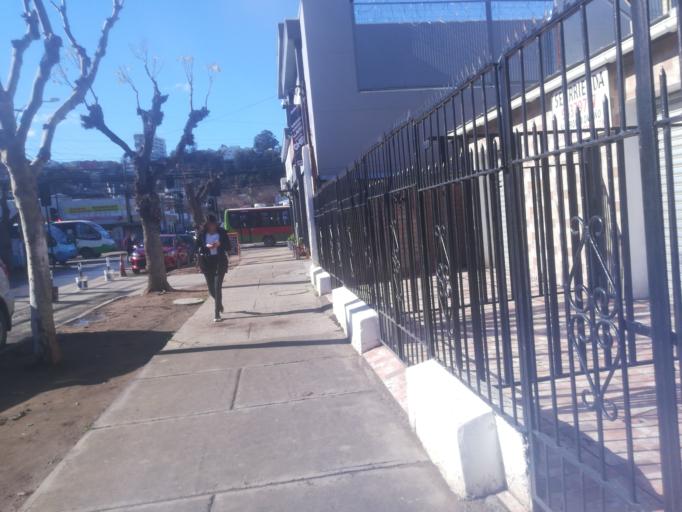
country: CL
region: Valparaiso
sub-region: Provincia de Valparaiso
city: Vina del Mar
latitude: -33.0111
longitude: -71.5432
